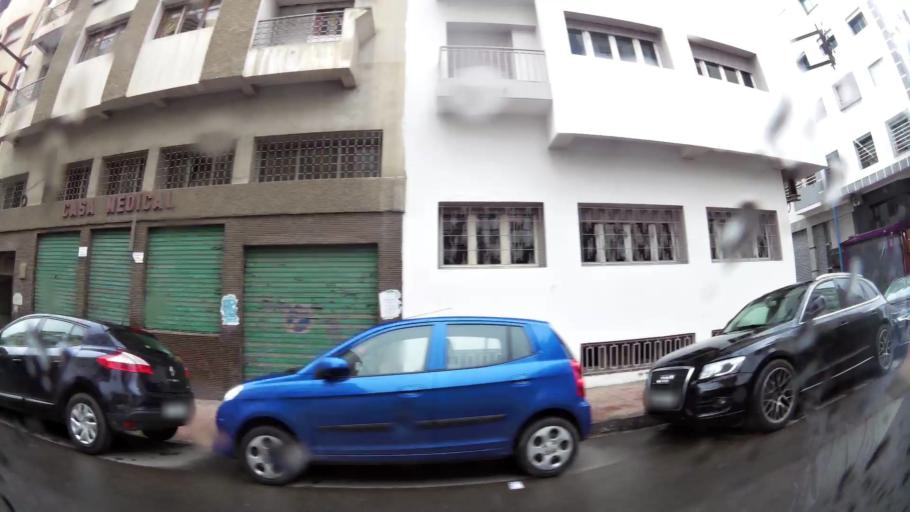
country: MA
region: Grand Casablanca
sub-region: Casablanca
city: Casablanca
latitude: 33.5743
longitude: -7.6130
